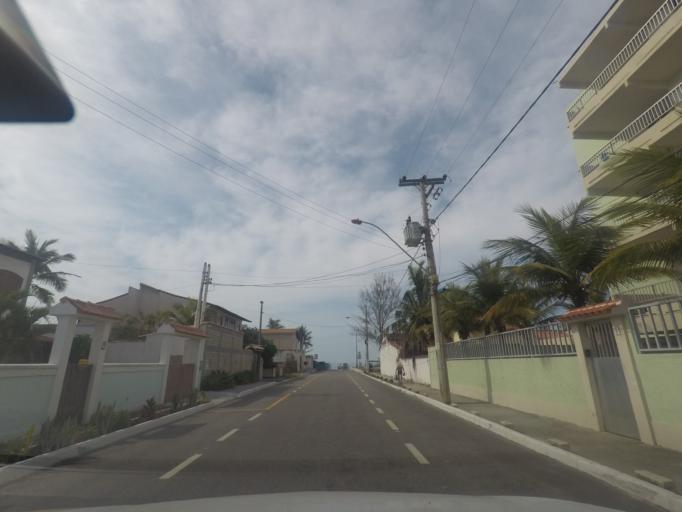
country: BR
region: Rio de Janeiro
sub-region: Marica
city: Marica
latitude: -22.9607
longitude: -42.8255
